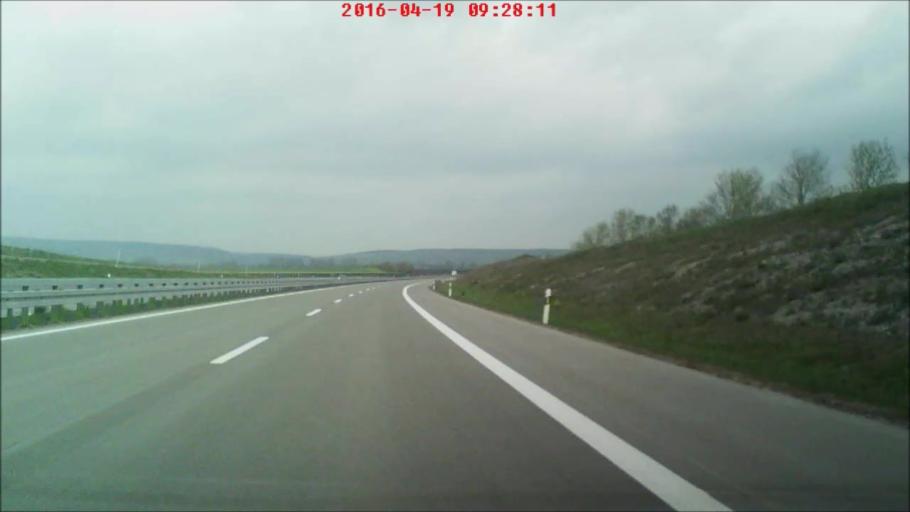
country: DE
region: Thuringia
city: Schillingstedt
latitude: 51.2280
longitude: 11.1834
